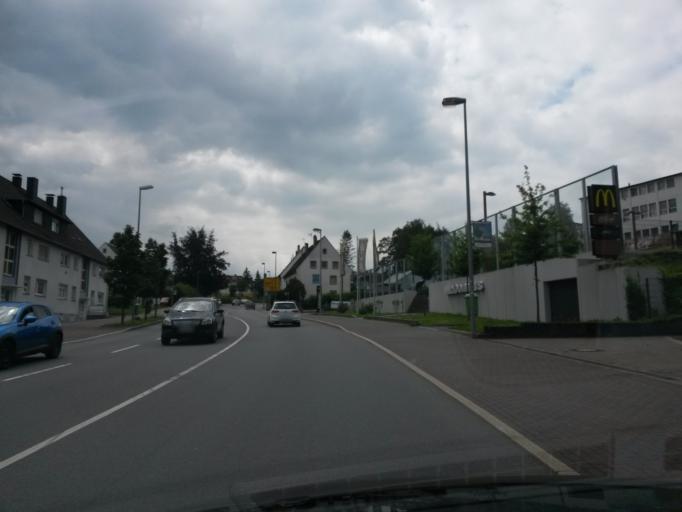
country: DE
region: North Rhine-Westphalia
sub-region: Regierungsbezirk Arnsberg
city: Luedenscheid
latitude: 51.2139
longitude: 7.6462
